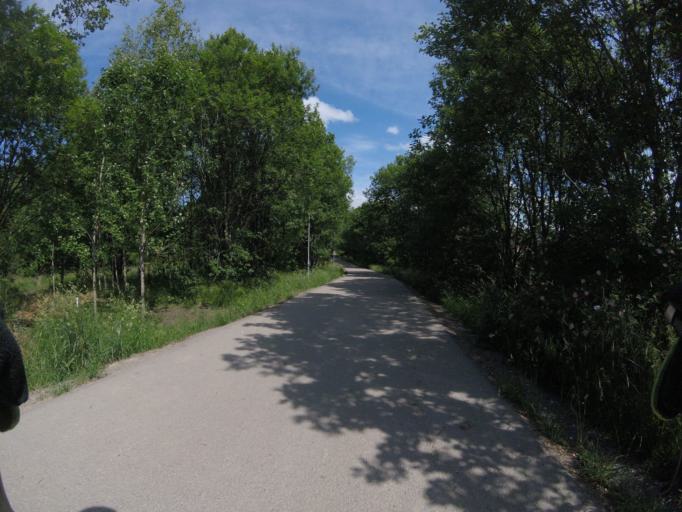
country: NO
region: Akershus
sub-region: Skedsmo
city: Lillestrom
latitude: 59.9833
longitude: 11.0340
